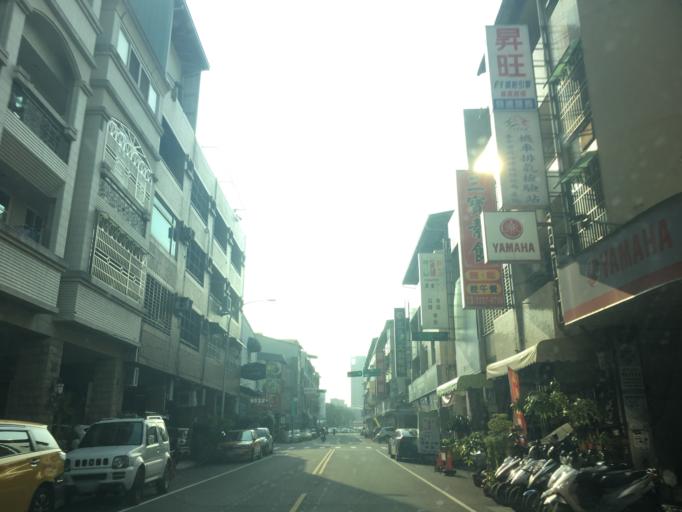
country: TW
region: Taiwan
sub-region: Taichung City
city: Taichung
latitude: 24.1707
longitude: 120.6868
